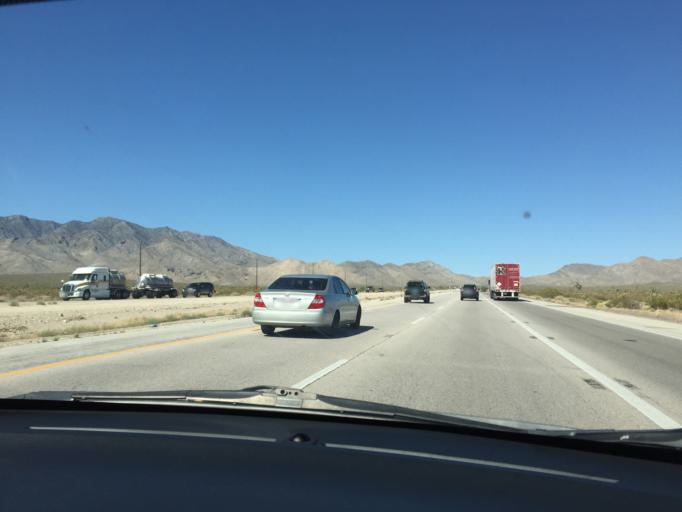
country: US
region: Nevada
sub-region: Clark County
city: Sandy Valley
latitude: 35.4553
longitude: -115.6418
